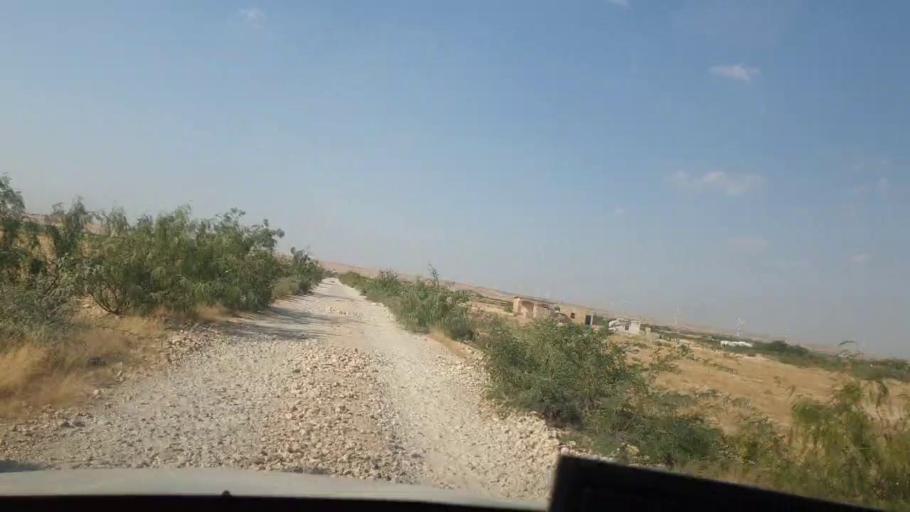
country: PK
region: Sindh
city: Daro Mehar
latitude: 25.0714
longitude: 68.0968
